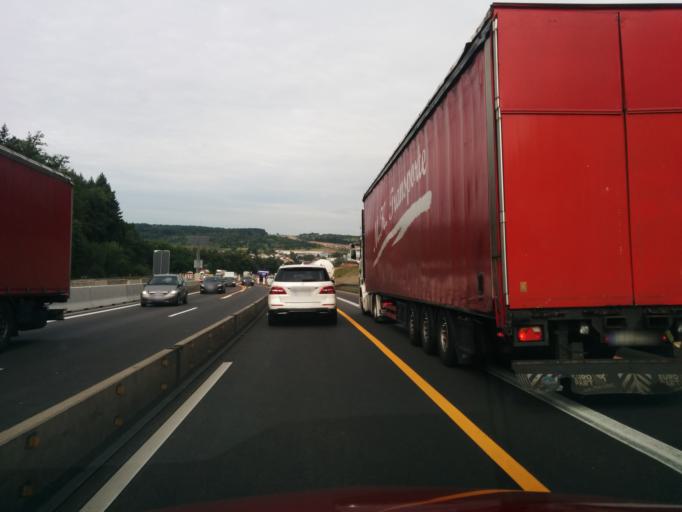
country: DE
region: Baden-Wuerttemberg
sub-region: Karlsruhe Region
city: Konigsbach-Stein
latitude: 48.9291
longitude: 8.5838
